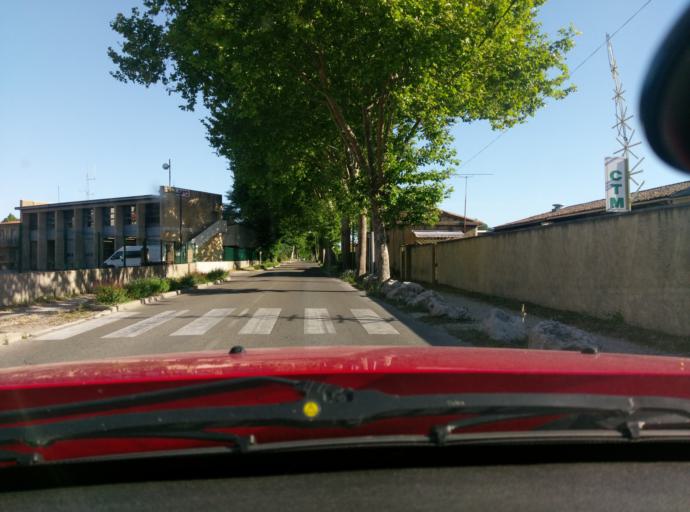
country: FR
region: Languedoc-Roussillon
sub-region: Departement du Gard
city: Uzes
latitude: 44.0194
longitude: 4.4157
